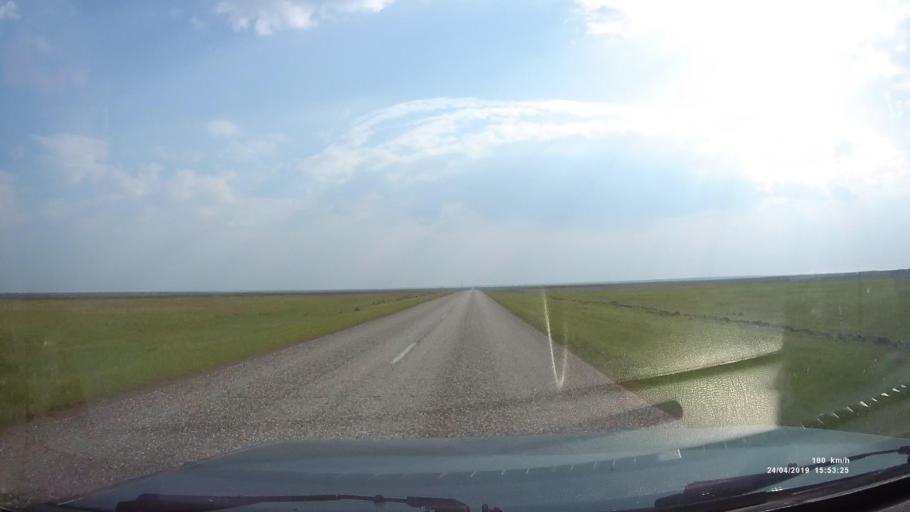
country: RU
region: Kalmykiya
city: Yashalta
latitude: 46.5986
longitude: 42.5760
